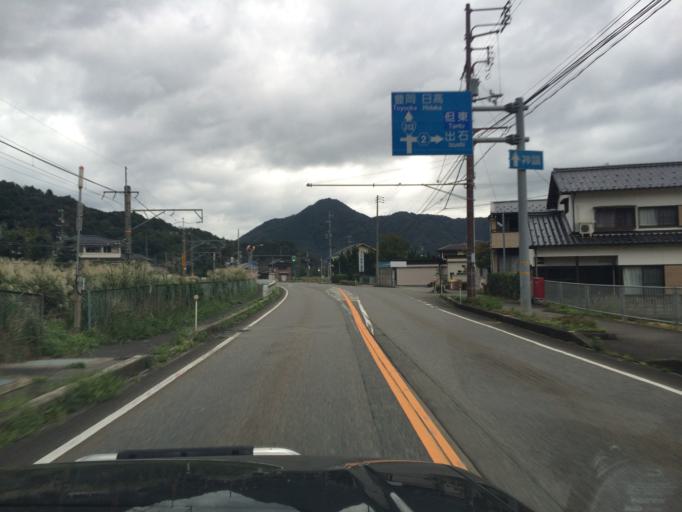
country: JP
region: Hyogo
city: Toyooka
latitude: 35.4233
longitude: 134.7902
